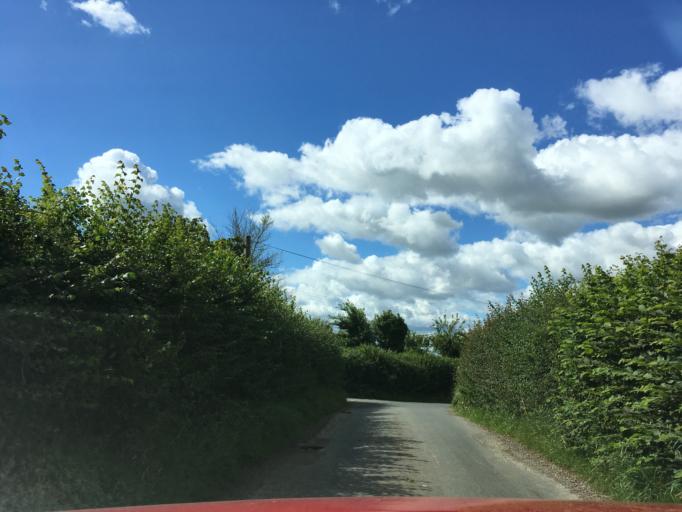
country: GB
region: England
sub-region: Gloucestershire
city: Newent
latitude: 51.8458
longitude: -2.3965
